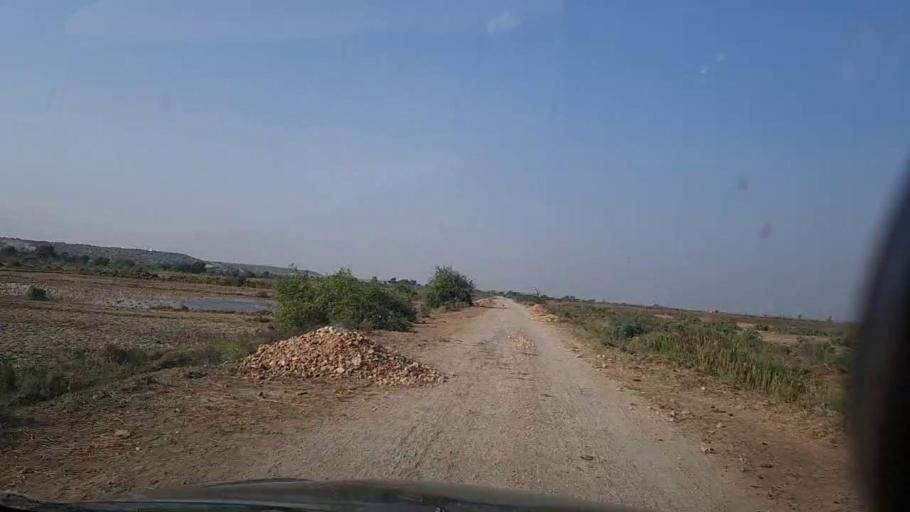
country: PK
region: Sindh
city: Thatta
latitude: 24.5891
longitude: 67.8764
